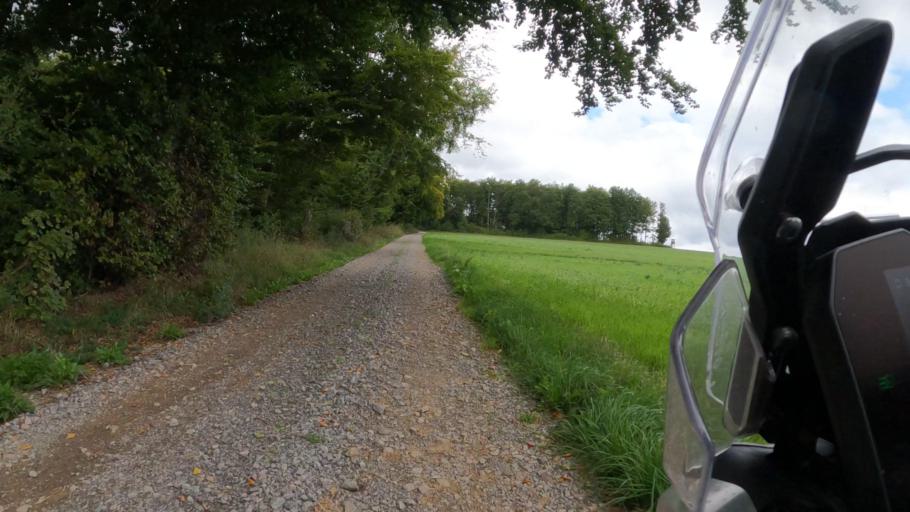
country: DE
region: Baden-Wuerttemberg
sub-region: Freiburg Region
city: Eggingen
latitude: 47.7057
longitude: 8.3656
